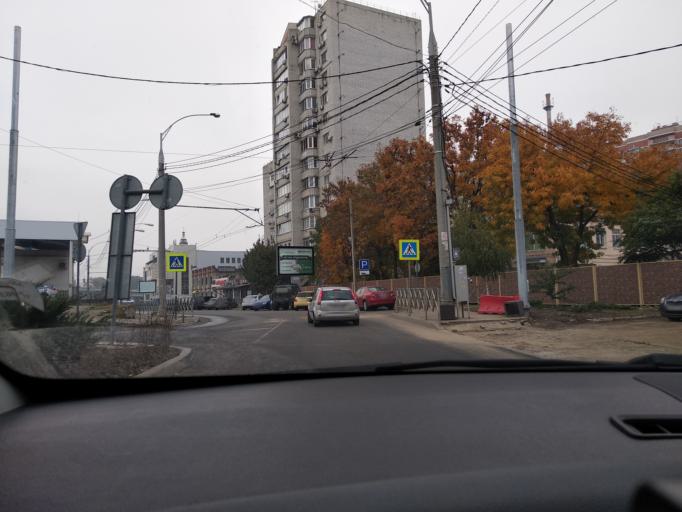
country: RU
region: Krasnodarskiy
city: Krasnodar
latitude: 45.0396
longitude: 38.9552
